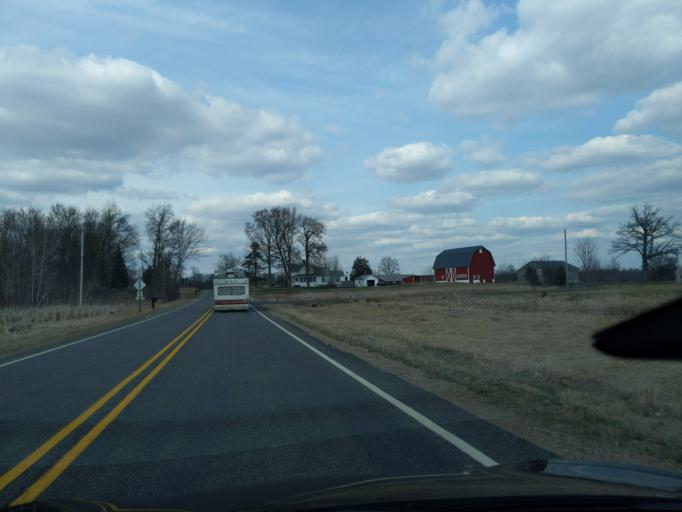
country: US
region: Michigan
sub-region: Ingham County
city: Leslie
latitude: 42.3662
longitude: -84.4194
